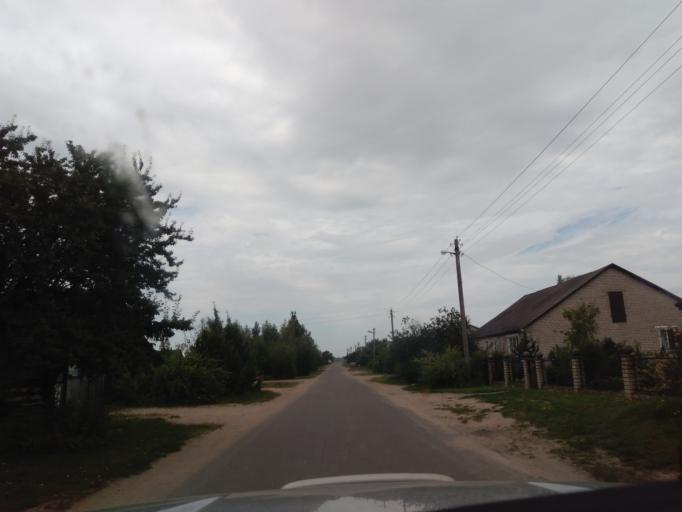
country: BY
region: Minsk
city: Kapyl'
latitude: 53.1551
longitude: 27.0705
